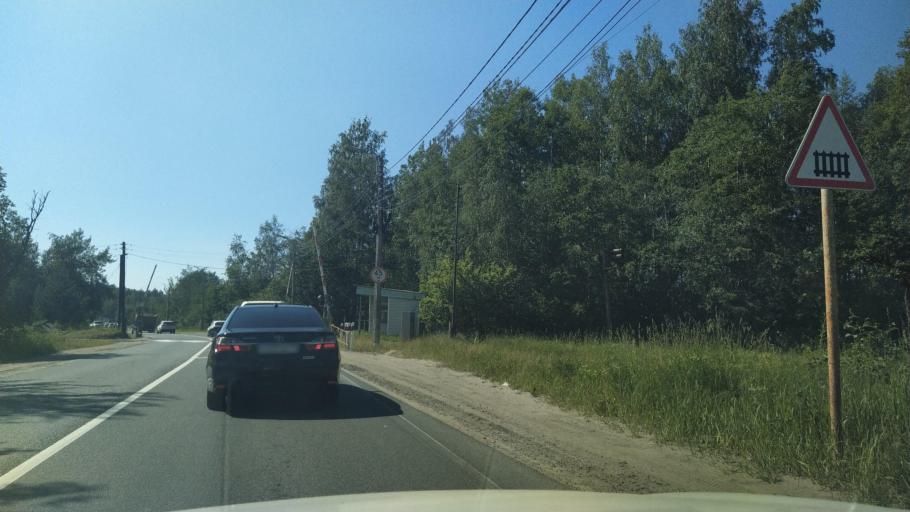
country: RU
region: St.-Petersburg
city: Beloostrov
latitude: 60.1416
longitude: 30.0244
